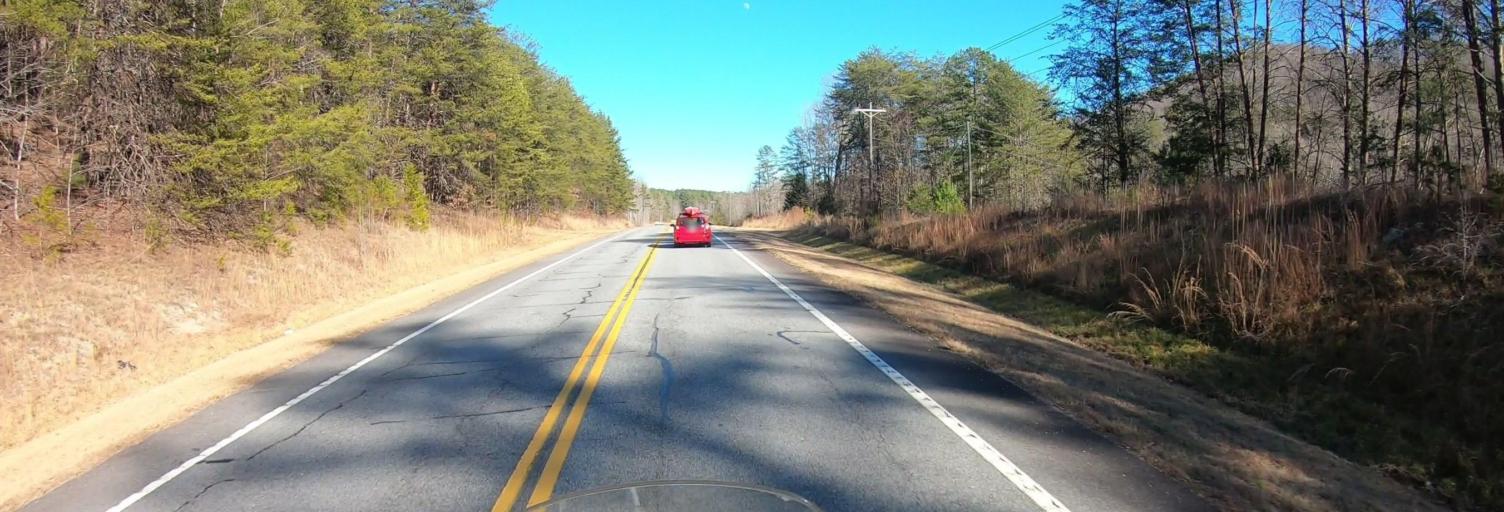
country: US
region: South Carolina
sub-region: Pickens County
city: Pickens
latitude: 34.9784
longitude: -82.7942
